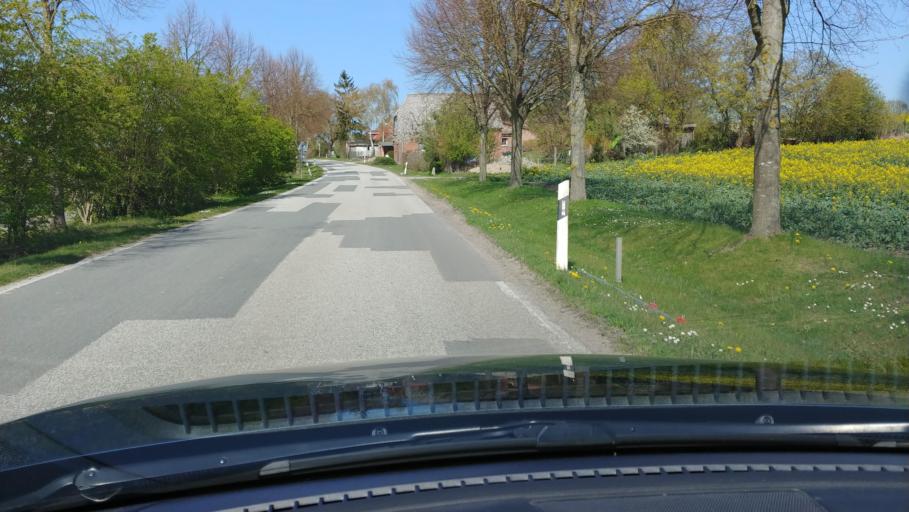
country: DE
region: Mecklenburg-Vorpommern
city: Muhlen Eichsen
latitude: 53.7824
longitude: 11.2658
